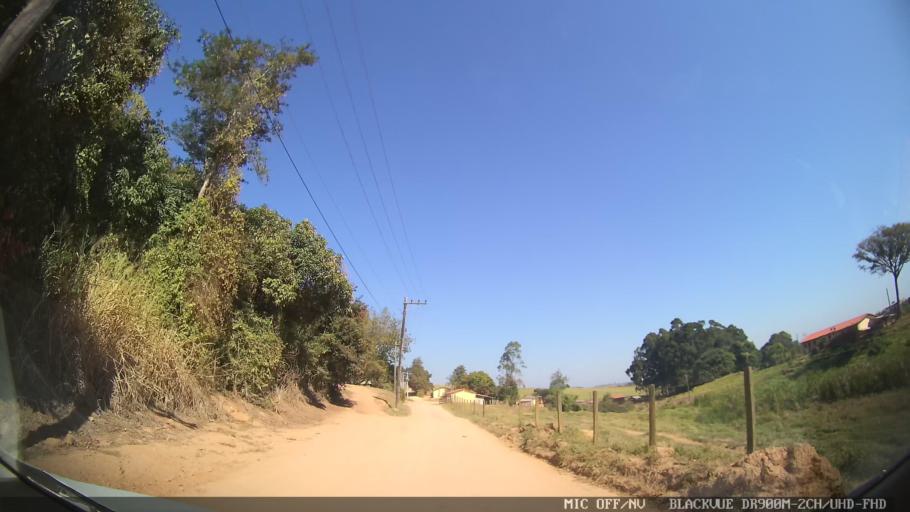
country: BR
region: Sao Paulo
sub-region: Itupeva
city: Itupeva
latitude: -23.1182
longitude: -47.0645
